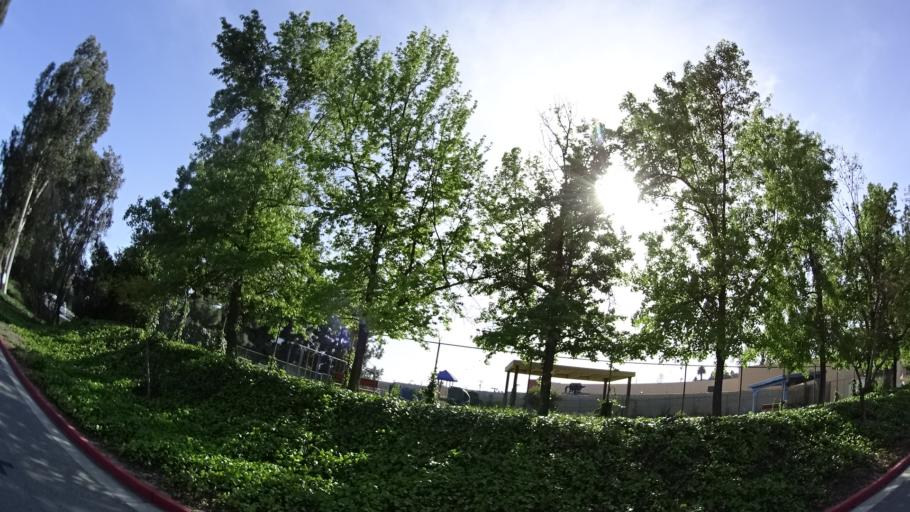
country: US
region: California
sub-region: Los Angeles County
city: Belvedere
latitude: 34.0641
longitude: -118.1719
